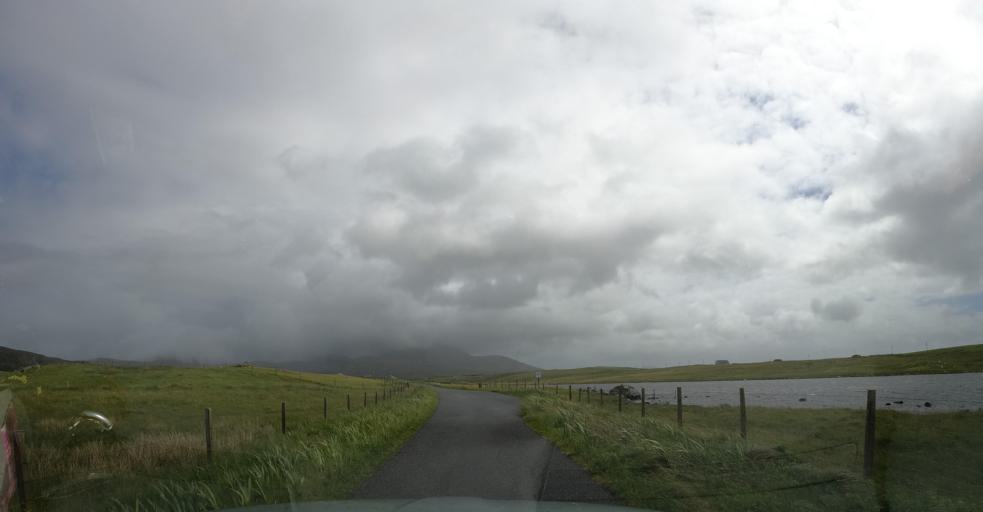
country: GB
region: Scotland
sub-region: Eilean Siar
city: Isle of South Uist
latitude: 57.2934
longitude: -7.3832
